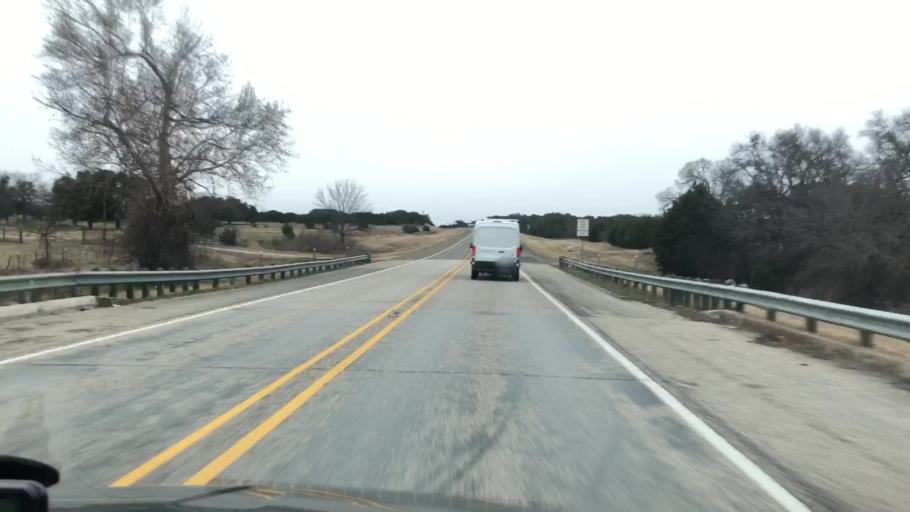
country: US
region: Texas
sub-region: Lampasas County
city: Lampasas
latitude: 31.1645
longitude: -98.1762
